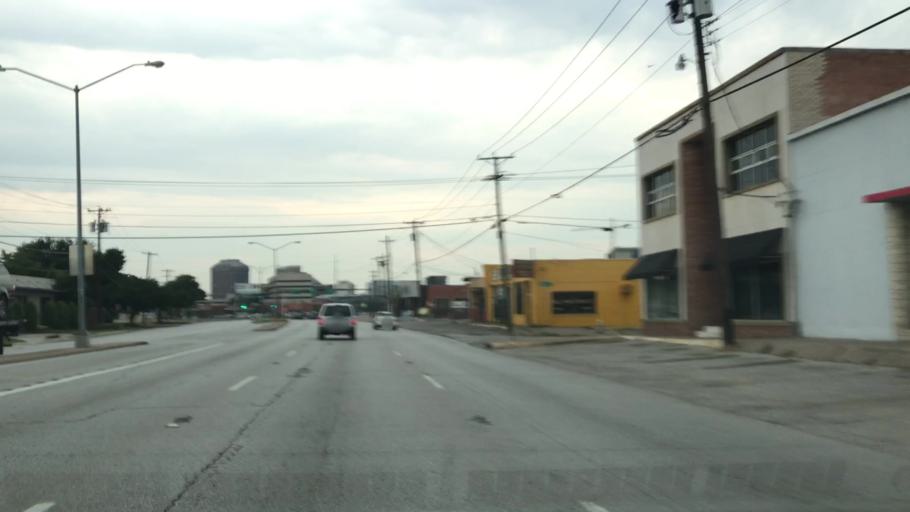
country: US
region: Texas
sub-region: Dallas County
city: Dallas
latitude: 32.7896
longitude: -96.8199
